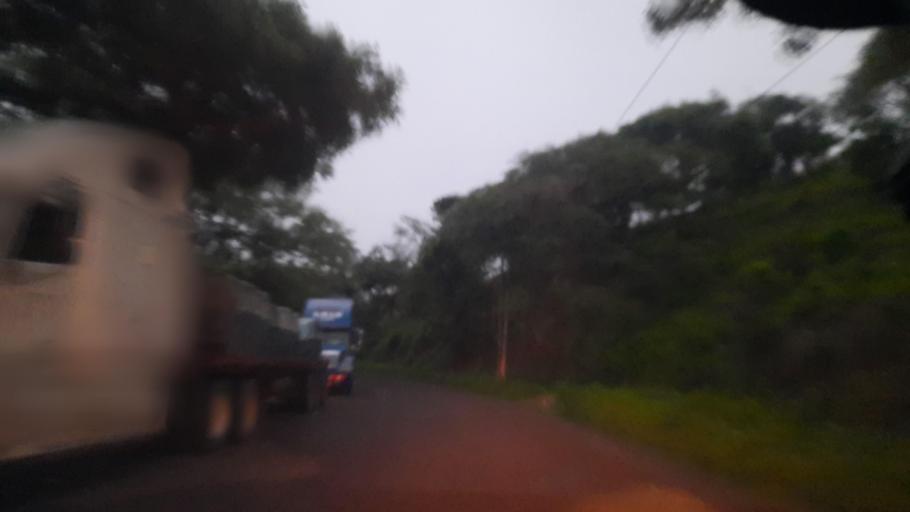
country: GT
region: Jutiapa
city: Atescatempa
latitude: 14.2173
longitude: -89.6901
